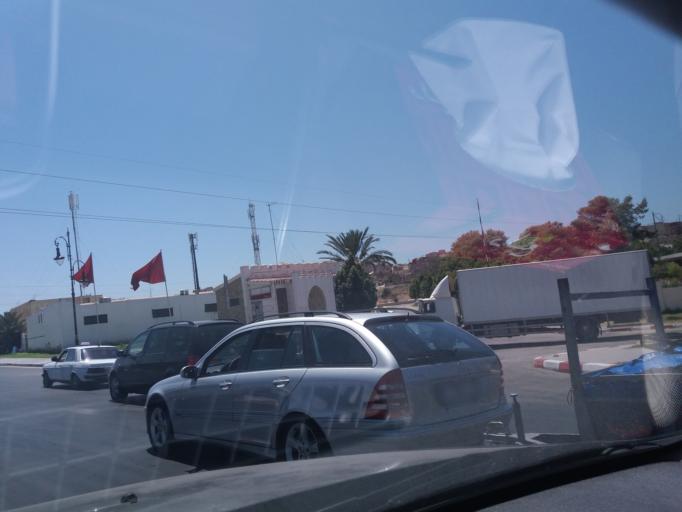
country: MA
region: Tanger-Tetouan
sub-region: Tanger-Assilah
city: Tangier
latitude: 35.7352
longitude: -5.7659
